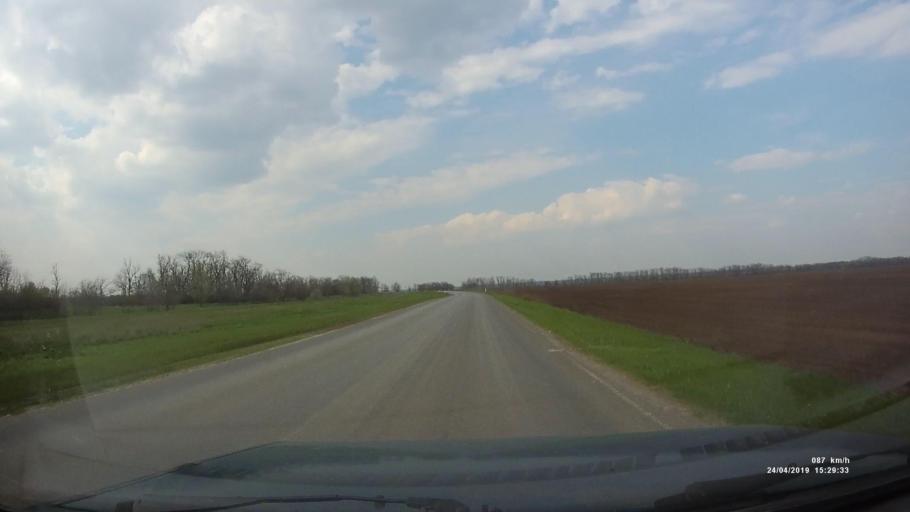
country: RU
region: Rostov
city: Remontnoye
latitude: 46.5951
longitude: 43.0179
